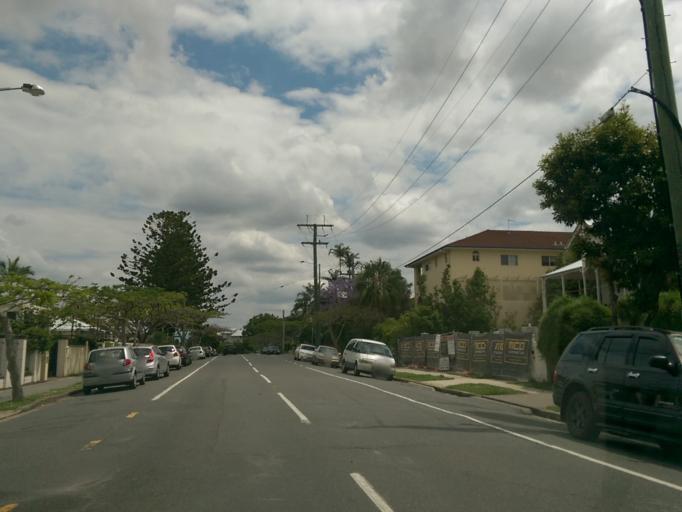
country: AU
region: Queensland
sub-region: Brisbane
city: Balmoral
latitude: -27.4714
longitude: 153.0508
